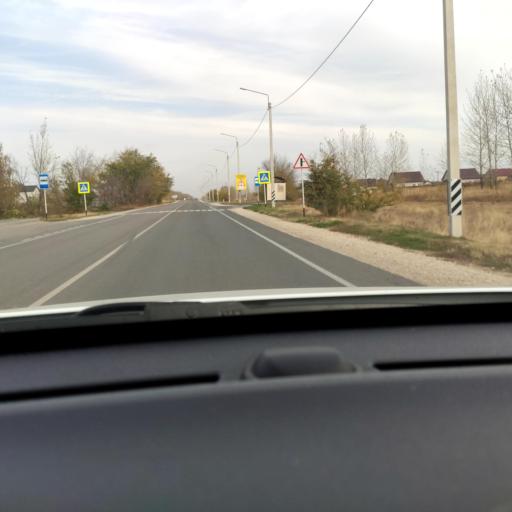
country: RU
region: Voronezj
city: Novaya Usman'
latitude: 51.6618
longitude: 39.4437
